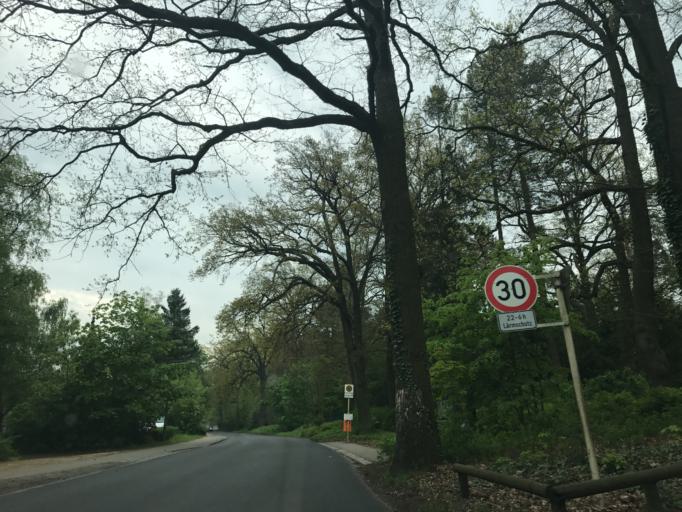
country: DE
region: Berlin
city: Falkenhagener Feld
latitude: 52.5581
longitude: 13.1823
